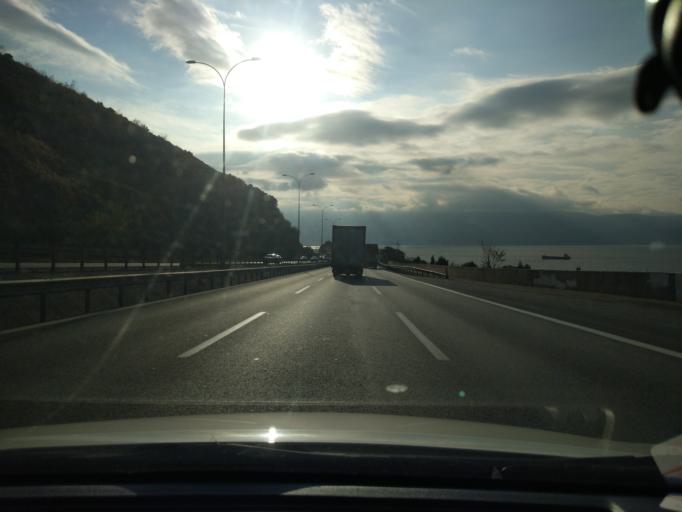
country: TR
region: Kocaeli
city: Hereke
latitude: 40.7818
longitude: 29.6277
